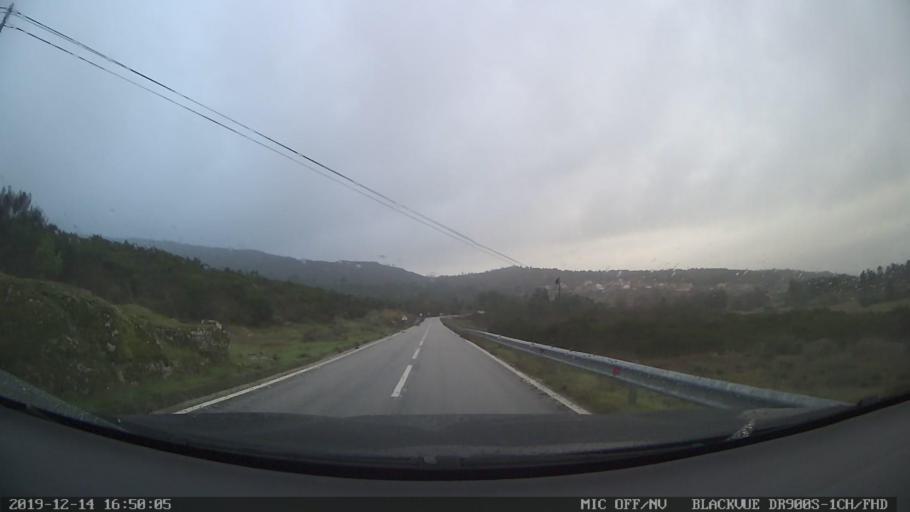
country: PT
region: Vila Real
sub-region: Murca
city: Murca
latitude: 41.4137
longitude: -7.5020
